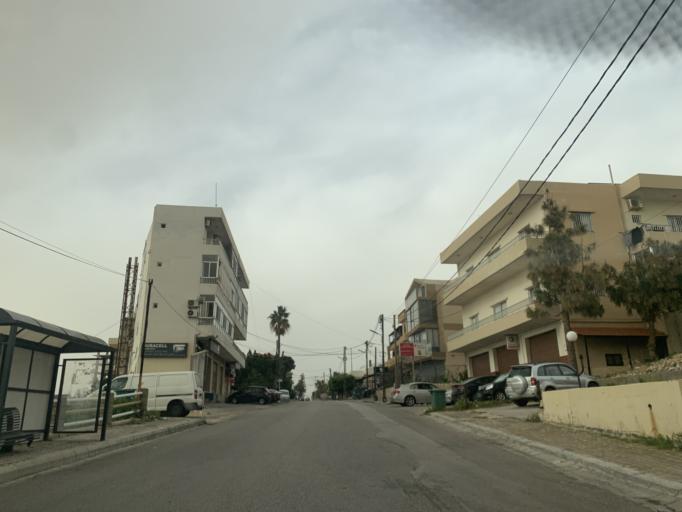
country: LB
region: Mont-Liban
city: Jbail
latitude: 34.0875
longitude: 35.6509
